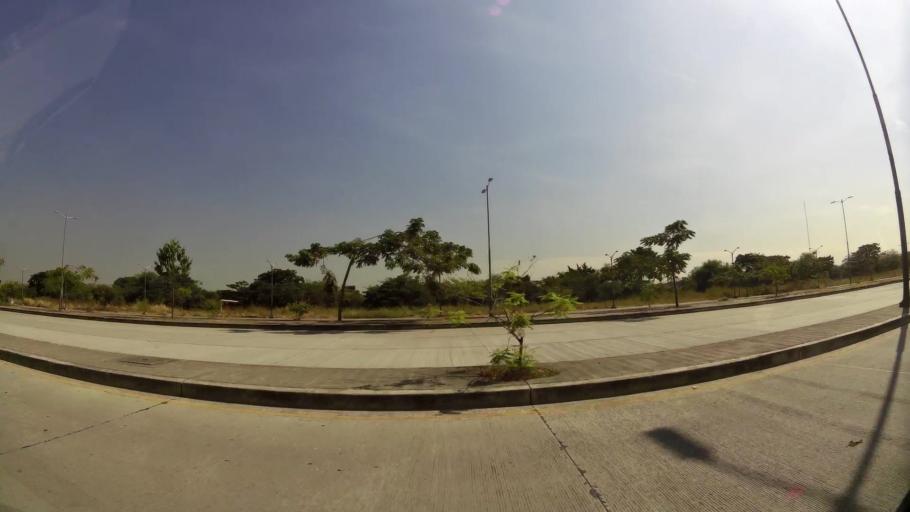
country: EC
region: Guayas
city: Eloy Alfaro
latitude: -2.1016
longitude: -79.9039
